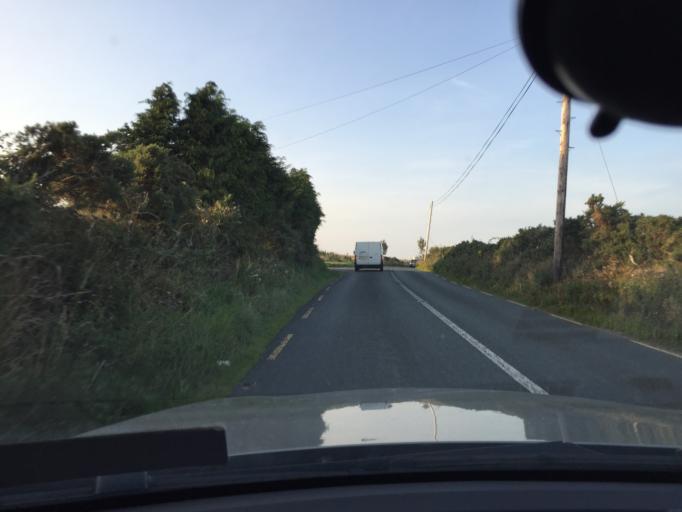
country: IE
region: Leinster
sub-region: Wicklow
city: Kilmacanoge
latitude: 53.1333
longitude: -6.1768
